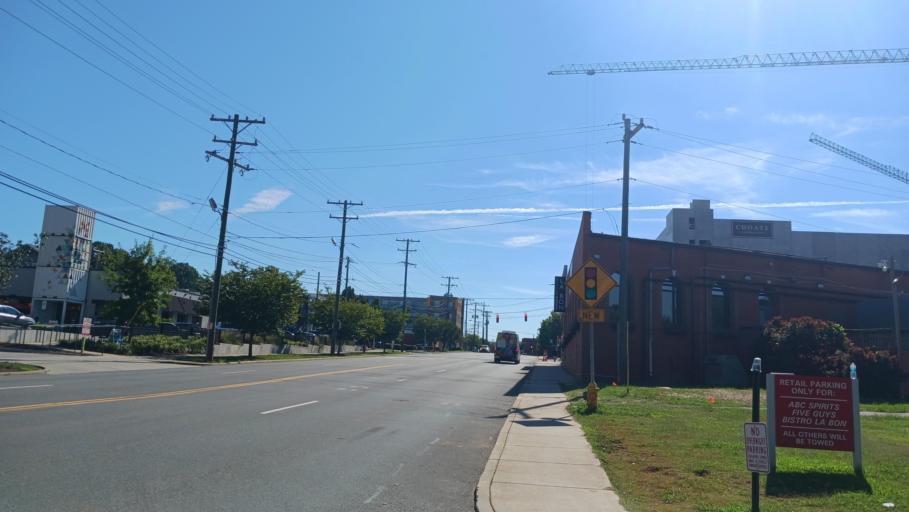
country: US
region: North Carolina
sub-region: Mecklenburg County
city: Charlotte
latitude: 35.2208
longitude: -80.8163
